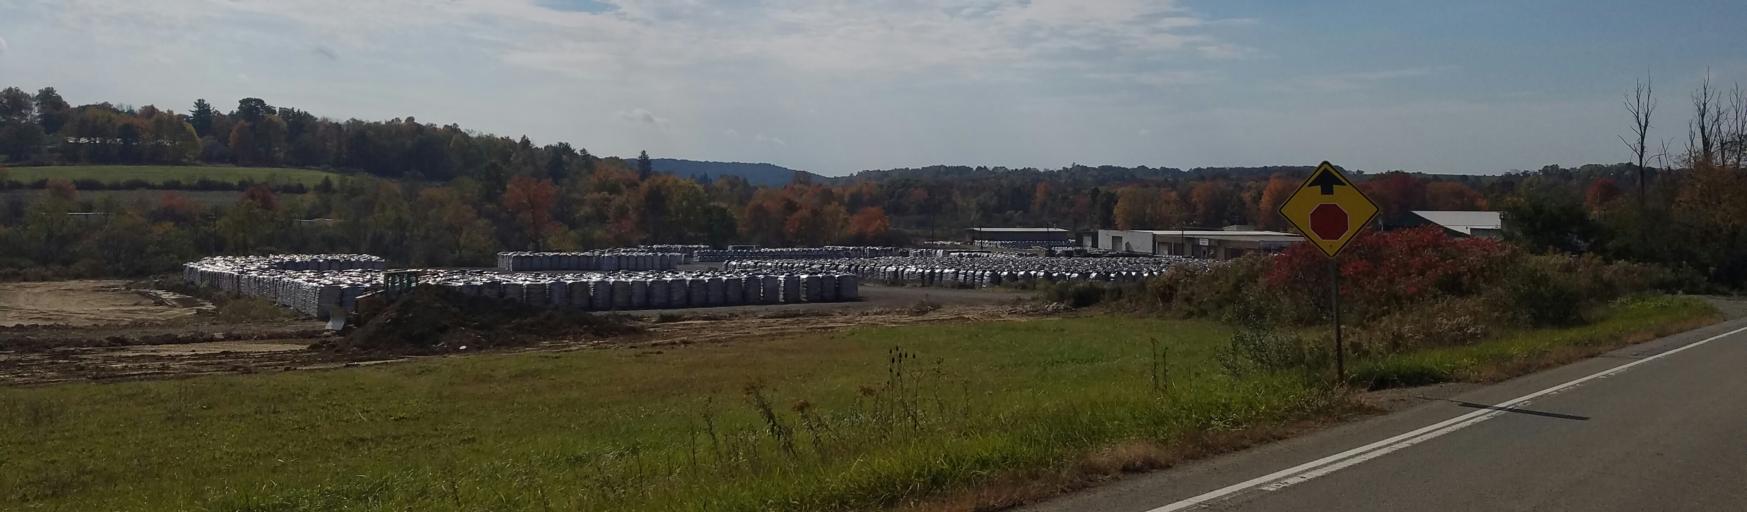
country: US
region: Pennsylvania
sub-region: Clarion County
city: Knox
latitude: 41.2072
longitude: -79.6582
